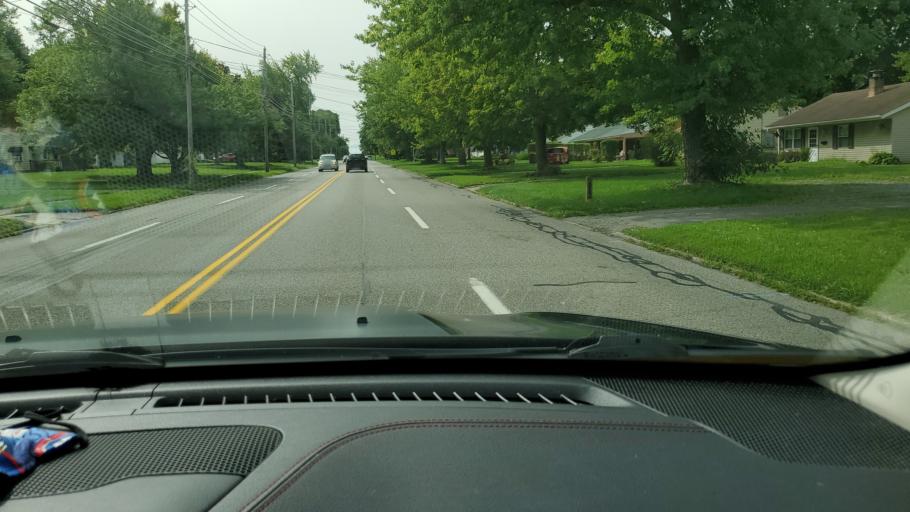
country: US
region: Ohio
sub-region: Mahoning County
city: Boardman
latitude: 41.0200
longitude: -80.6723
